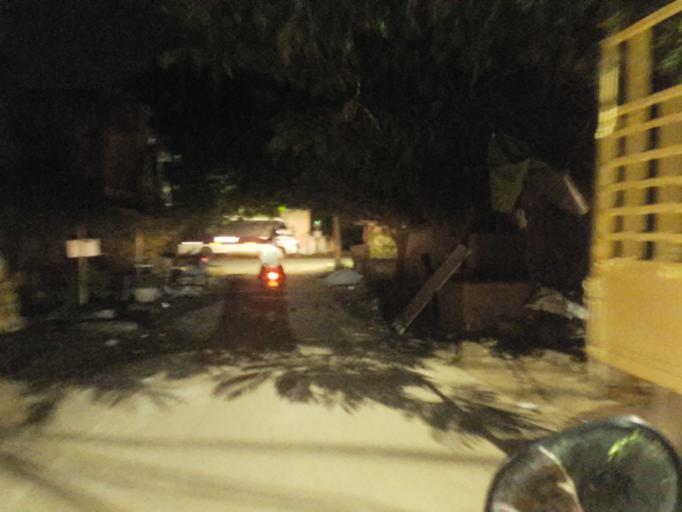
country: IN
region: Telangana
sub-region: Rangareddi
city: Kukatpalli
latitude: 17.4853
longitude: 78.3927
